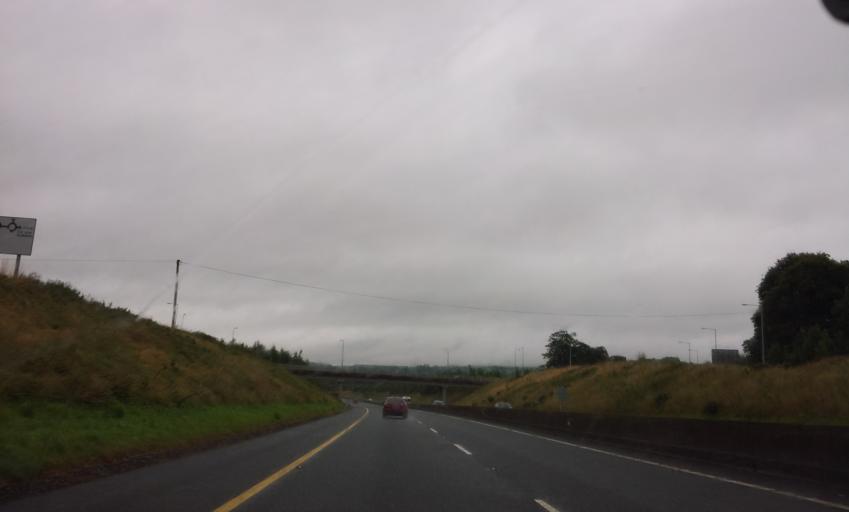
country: IE
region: Munster
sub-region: County Cork
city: Fermoy
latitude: 52.1601
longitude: -8.2658
